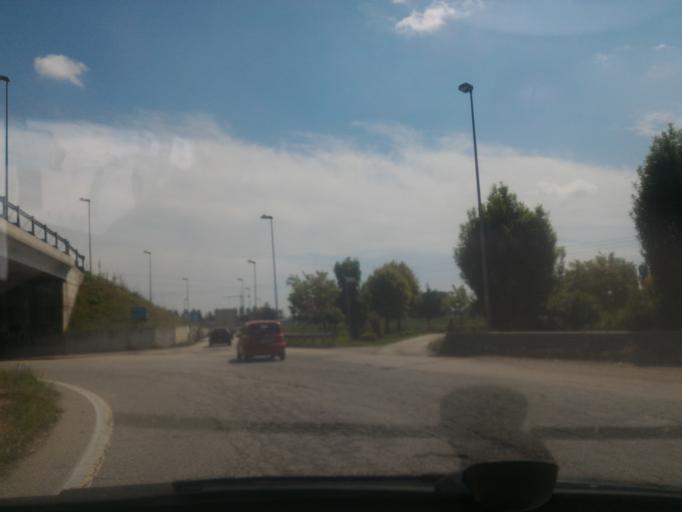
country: IT
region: Piedmont
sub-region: Provincia di Torino
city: Moncalieri
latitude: 44.9826
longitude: 7.7022
